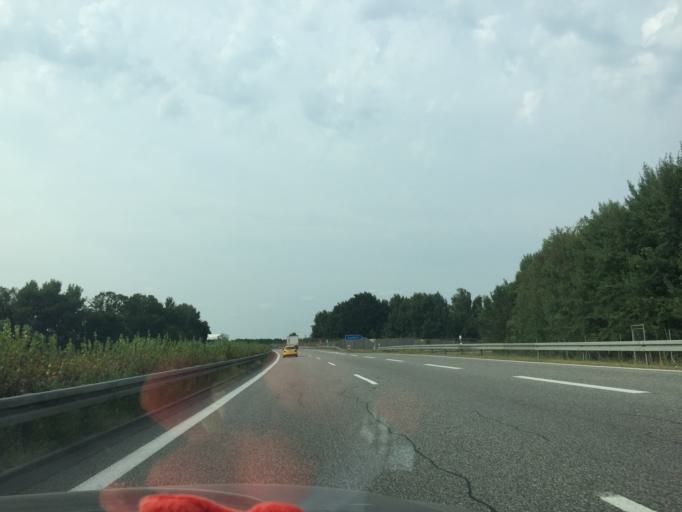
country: DE
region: Brandenburg
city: Schwerin
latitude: 52.1552
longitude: 13.6487
